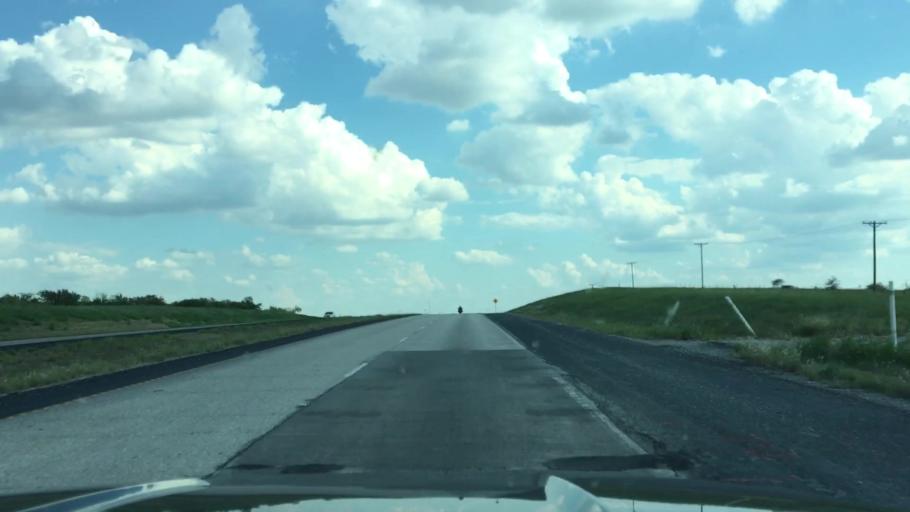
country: US
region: Texas
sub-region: Wise County
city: New Fairview
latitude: 33.1299
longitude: -97.4924
